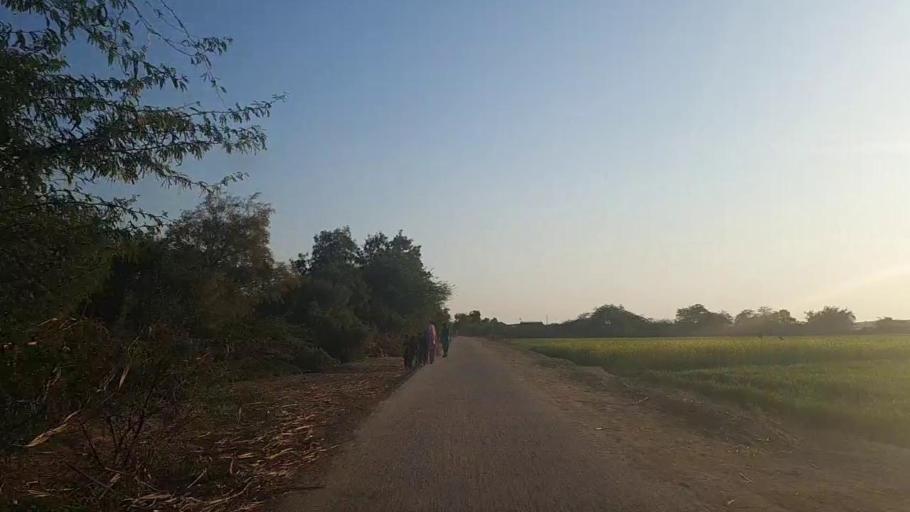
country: PK
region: Sindh
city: Jam Sahib
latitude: 26.3335
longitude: 68.6983
